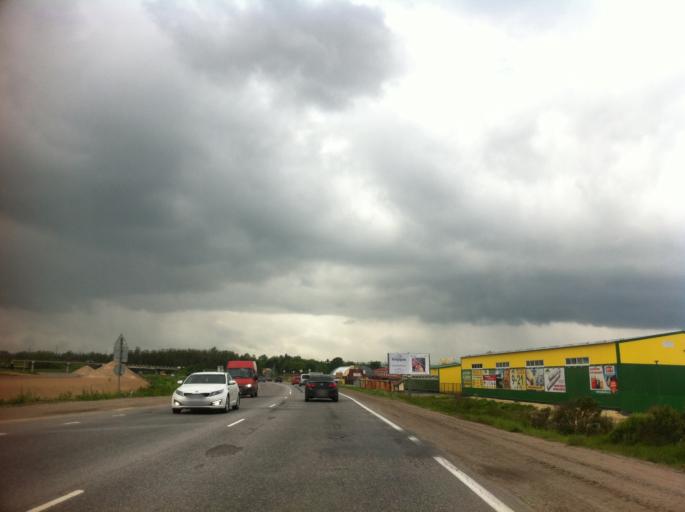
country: RU
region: Leningrad
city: Mariyenburg
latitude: 59.5259
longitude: 30.0813
